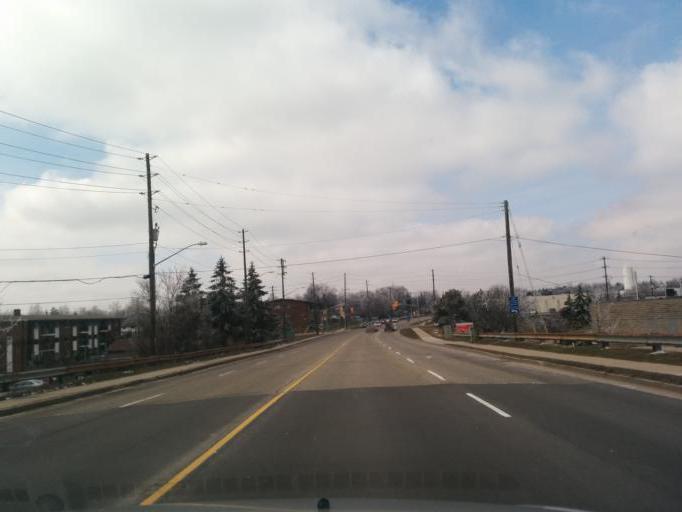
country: CA
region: Ontario
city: Waterloo
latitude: 43.4927
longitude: -80.5427
